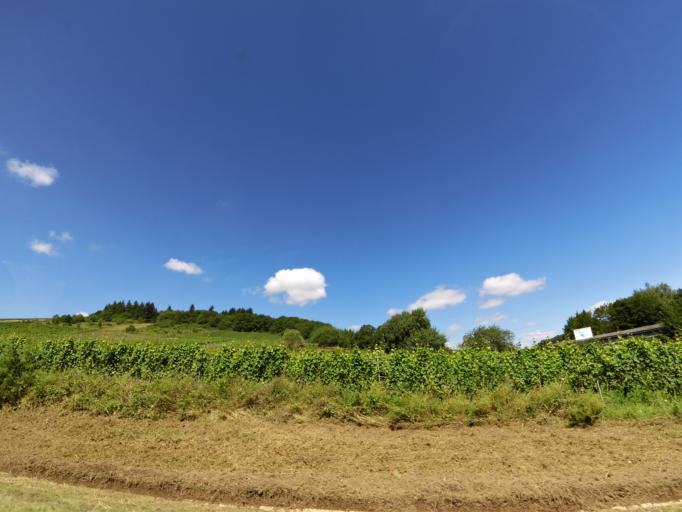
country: DE
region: Rheinland-Pfalz
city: Osann-Monzel
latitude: 49.9215
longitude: 6.9323
